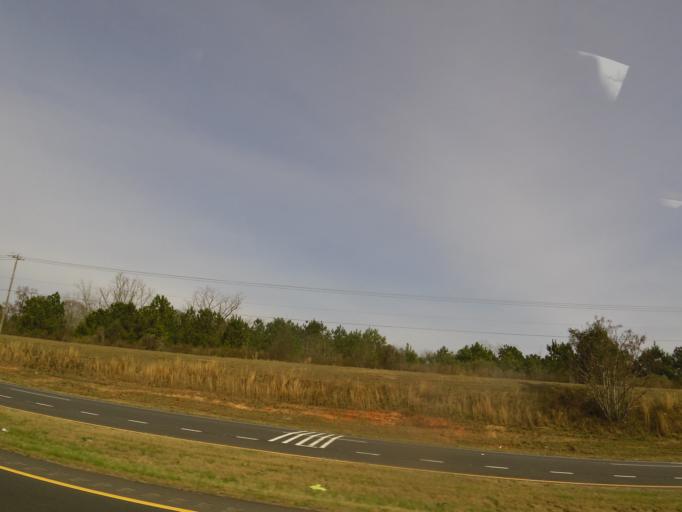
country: US
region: Alabama
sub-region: Dale County
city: Midland City
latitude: 31.2854
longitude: -85.4665
